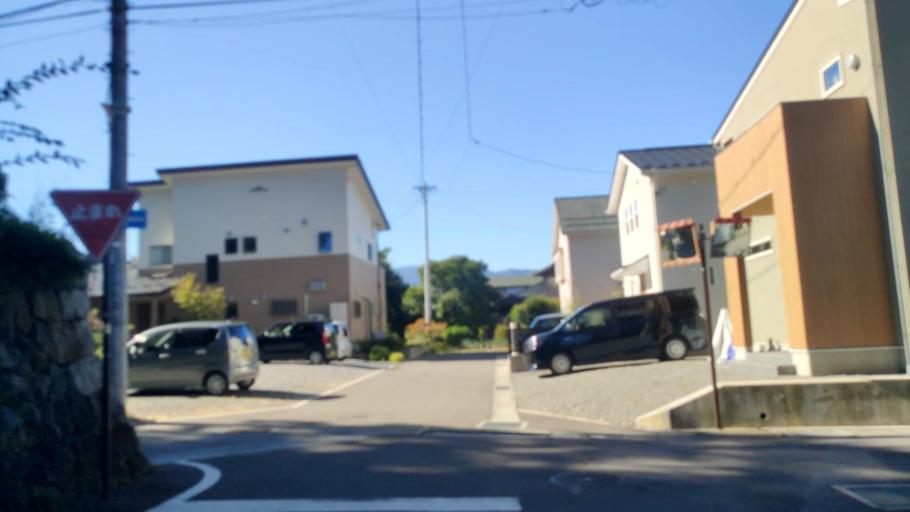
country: JP
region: Nagano
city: Suwa
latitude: 36.0386
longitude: 138.1116
